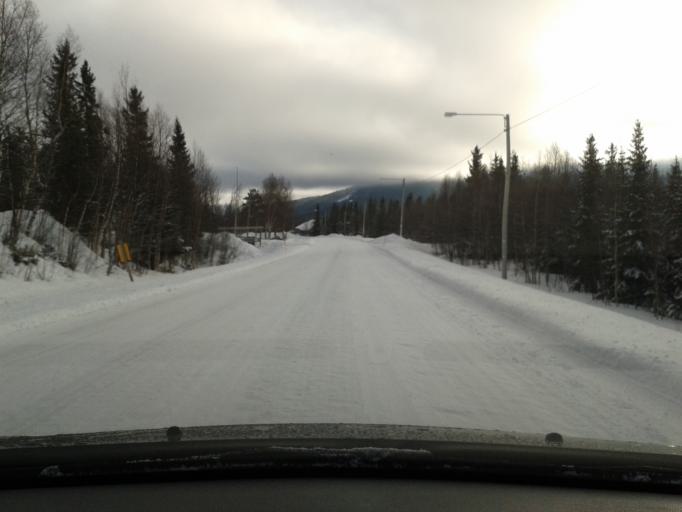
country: SE
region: Vaesterbotten
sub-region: Vilhelmina Kommun
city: Sjoberg
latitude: 65.2537
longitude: 15.5322
